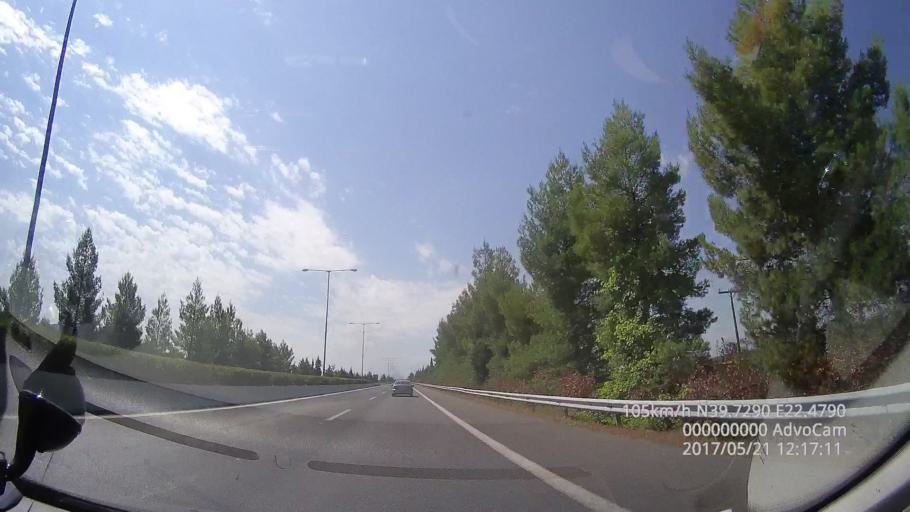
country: GR
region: Thessaly
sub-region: Nomos Larisis
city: Makrychori
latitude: 39.7285
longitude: 22.4791
